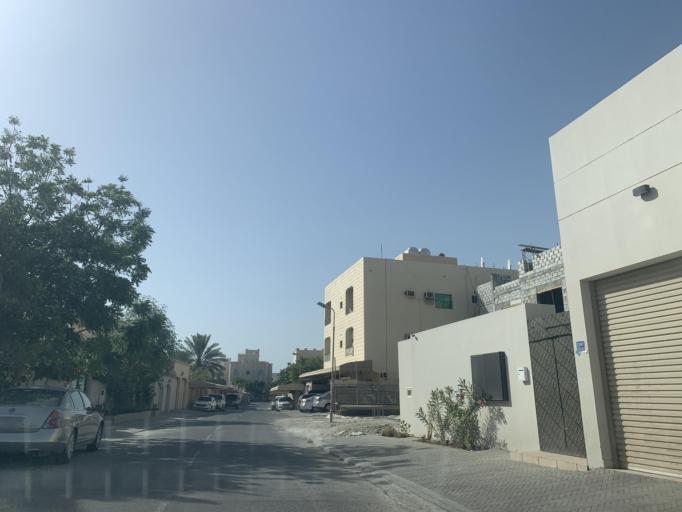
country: BH
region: Northern
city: Madinat `Isa
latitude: 26.1640
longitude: 50.5730
